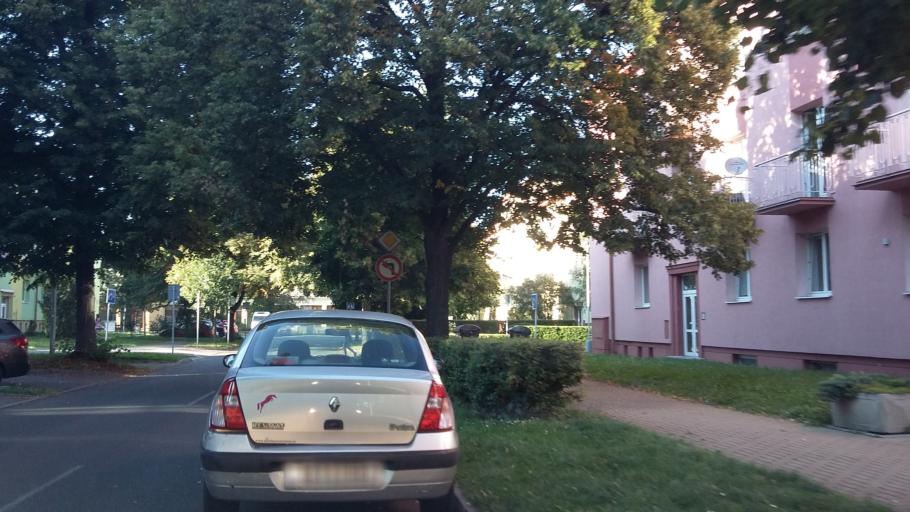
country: CZ
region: Praha
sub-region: Praha 19
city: Kbely
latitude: 50.1366
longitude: 14.5529
